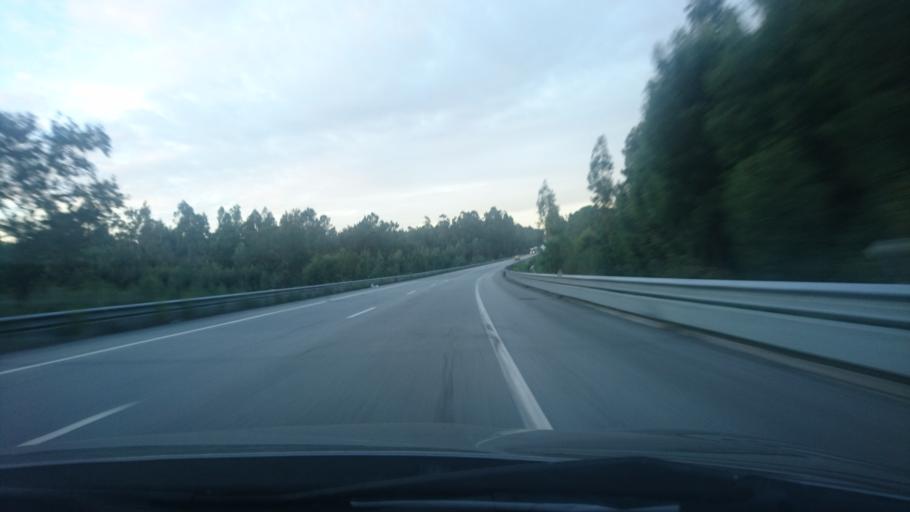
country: PT
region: Aveiro
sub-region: Santa Maria da Feira
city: Milheiros de Poiares
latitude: 40.9331
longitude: -8.4789
